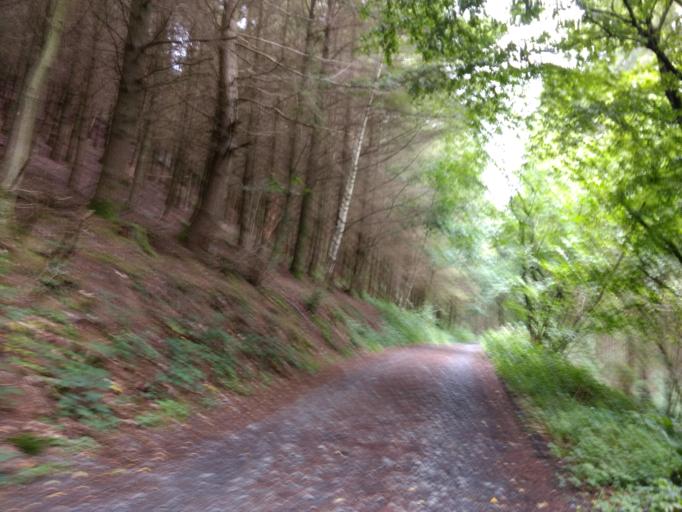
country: BE
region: Wallonia
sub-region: Province du Luxembourg
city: Houffalize
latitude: 50.1401
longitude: 5.7292
